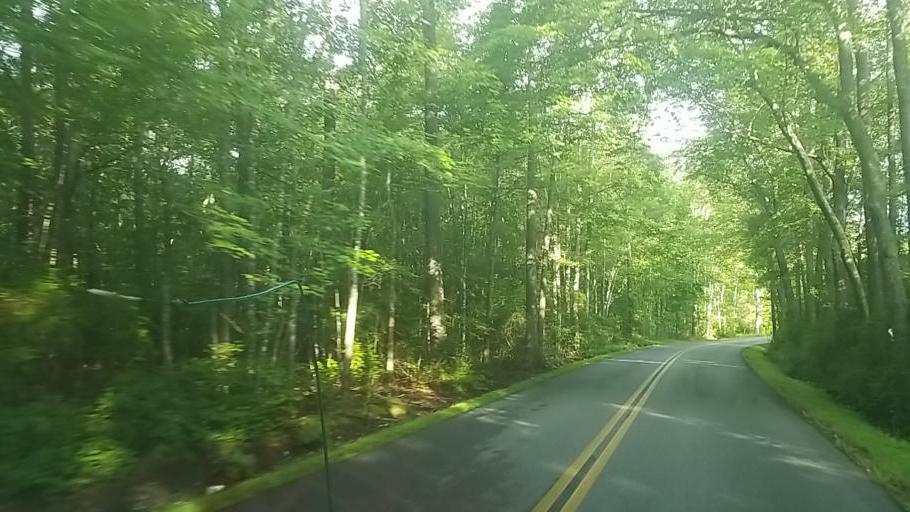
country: US
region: Maryland
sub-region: Worcester County
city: West Ocean City
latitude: 38.3237
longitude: -75.1506
